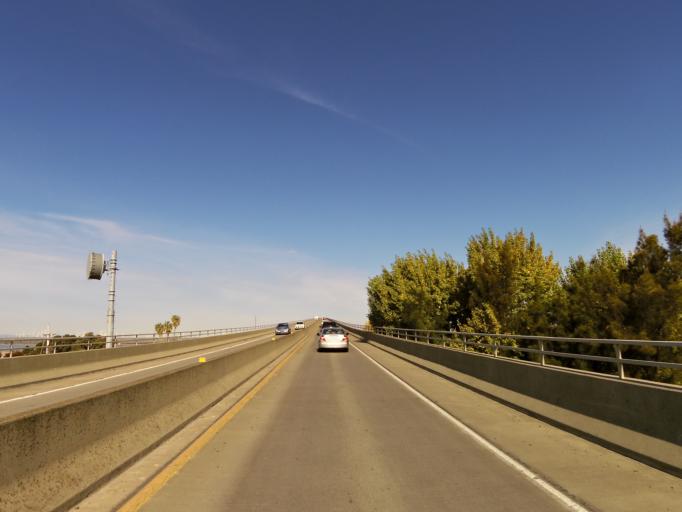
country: US
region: California
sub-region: Contra Costa County
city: Oakley
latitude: 38.0177
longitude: -121.7515
